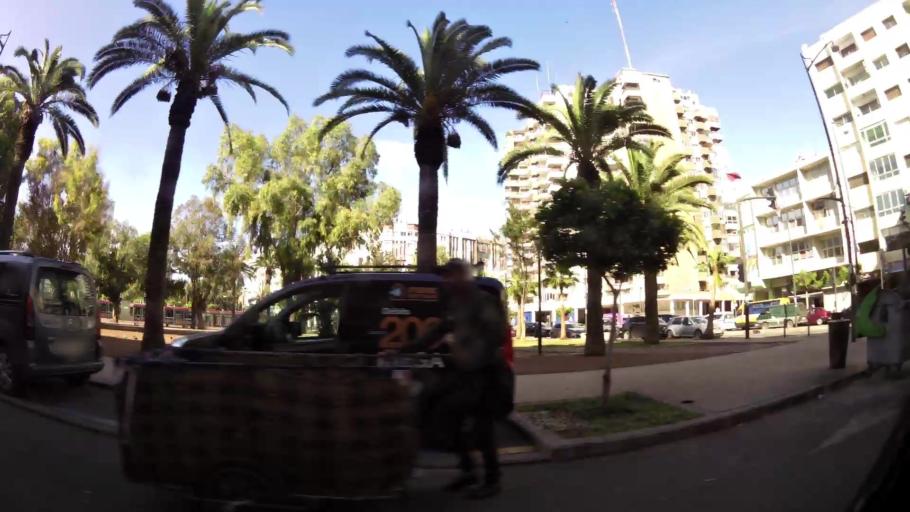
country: MA
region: Grand Casablanca
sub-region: Casablanca
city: Casablanca
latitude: 33.5911
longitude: -7.5917
